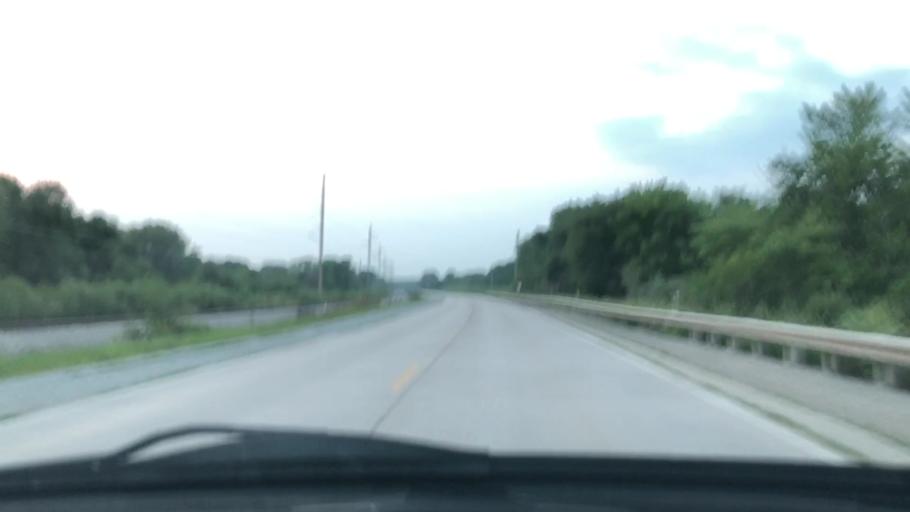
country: US
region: Iowa
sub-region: Johnson County
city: North Liberty
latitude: 41.7945
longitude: -91.6414
